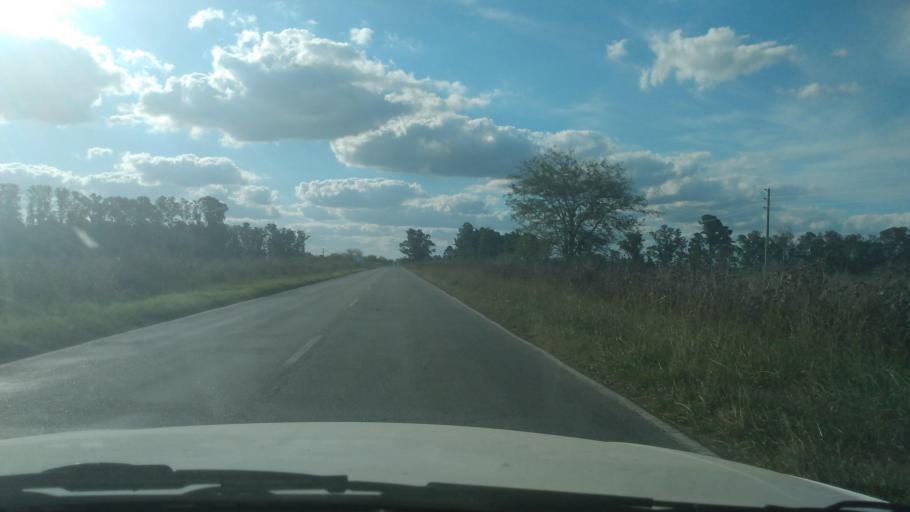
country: AR
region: Buenos Aires
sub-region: Partido de Mercedes
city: Mercedes
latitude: -34.7447
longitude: -59.3833
